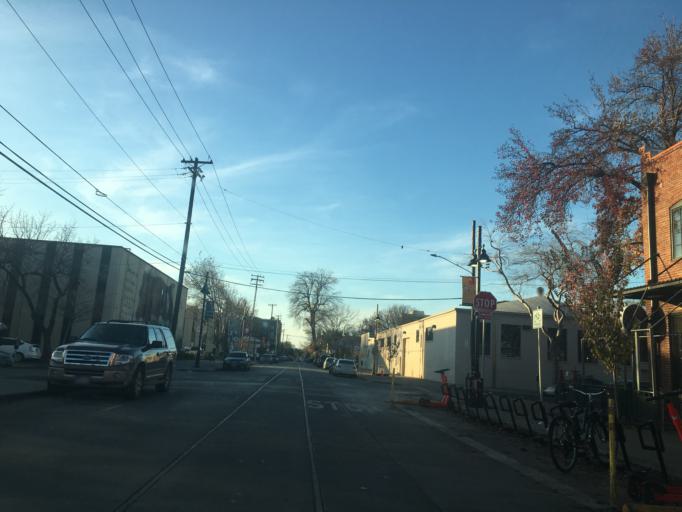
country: US
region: California
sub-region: Sacramento County
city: Sacramento
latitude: 38.5699
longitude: -121.4913
